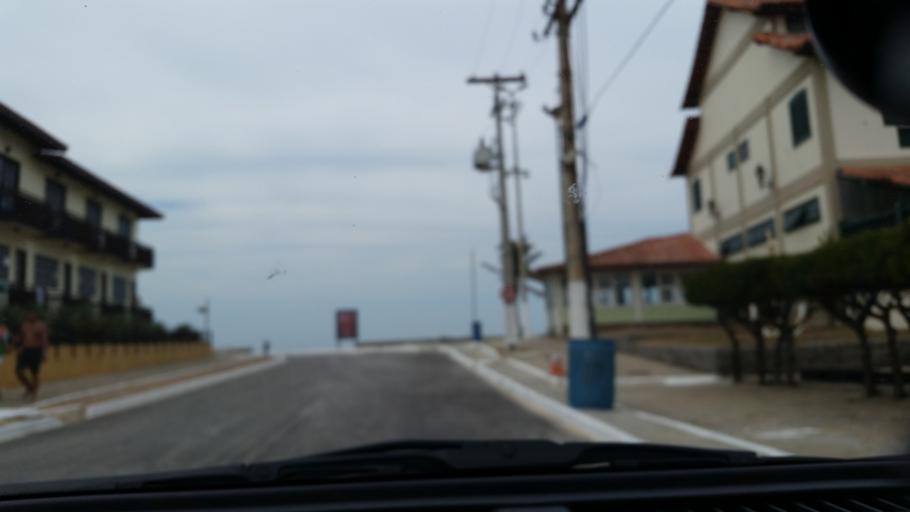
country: BR
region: Rio de Janeiro
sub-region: Cabo Frio
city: Cabo Frio
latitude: -22.8630
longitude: -41.9862
